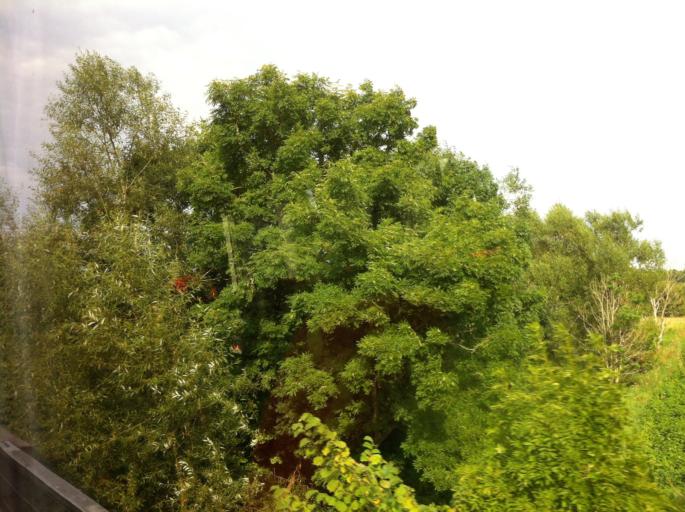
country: SE
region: Skane
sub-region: Kristianstads Kommun
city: Degeberga
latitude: 55.8976
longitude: 14.0802
